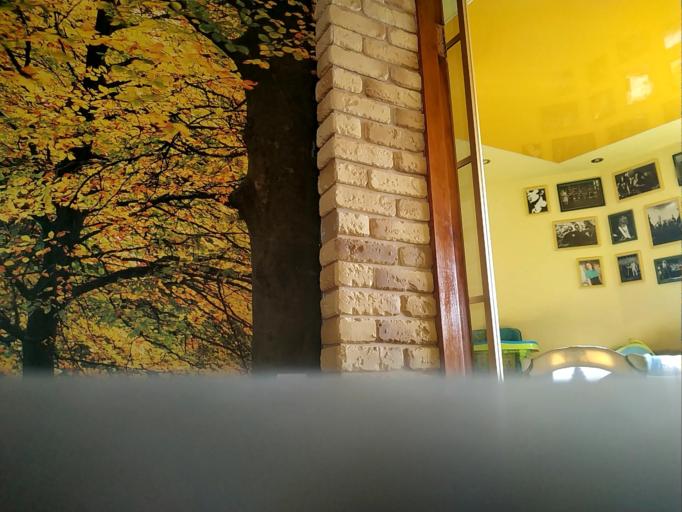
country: RU
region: Kaluga
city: Mosal'sk
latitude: 54.4879
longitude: 35.1322
